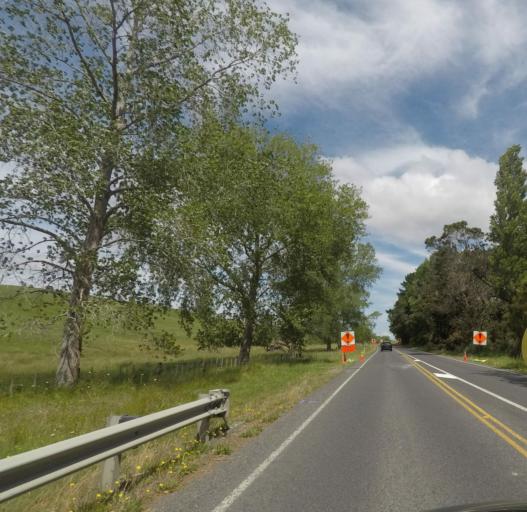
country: NZ
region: Auckland
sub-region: Auckland
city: Rothesay Bay
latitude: -36.6663
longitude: 174.6788
